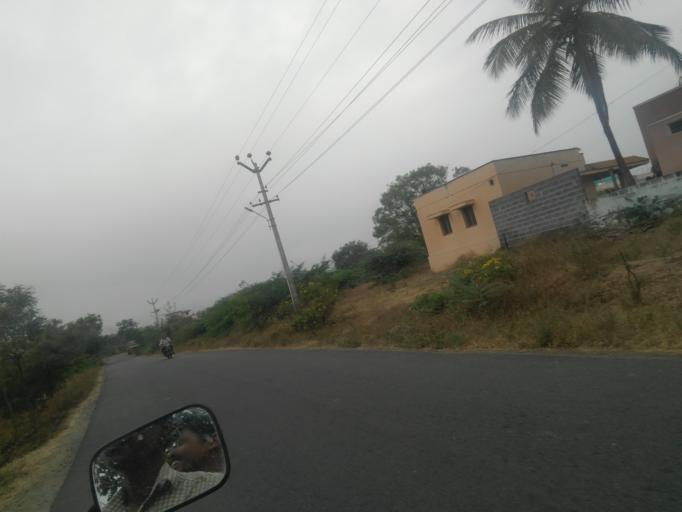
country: IN
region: Tamil Nadu
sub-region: Coimbatore
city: Karamadai
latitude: 11.2603
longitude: 76.9473
